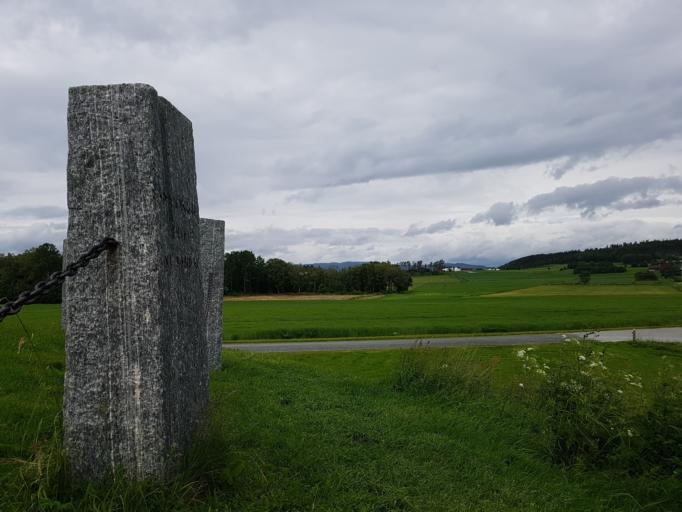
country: NO
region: Nord-Trondelag
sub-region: Frosta
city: Frosta
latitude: 63.5685
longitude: 10.7044
